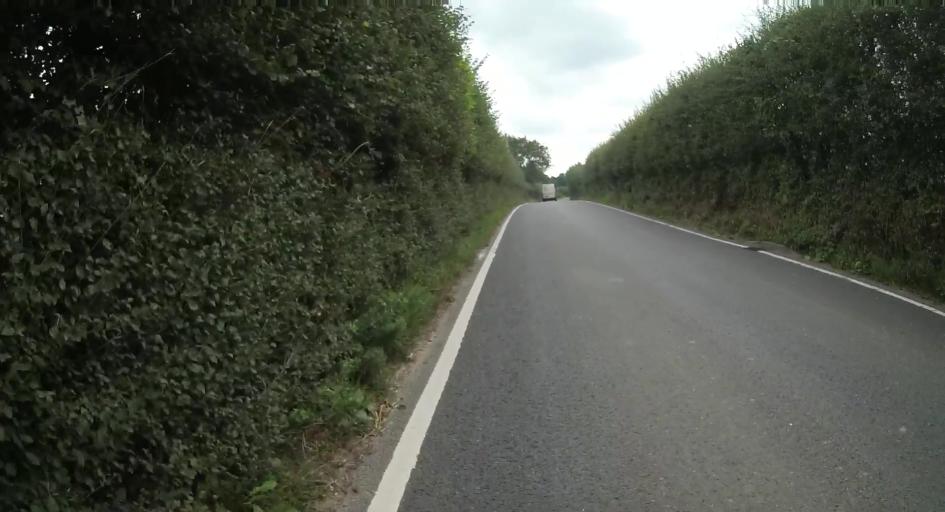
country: GB
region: England
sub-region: Isle of Wight
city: Niton
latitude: 50.6197
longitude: -1.2651
